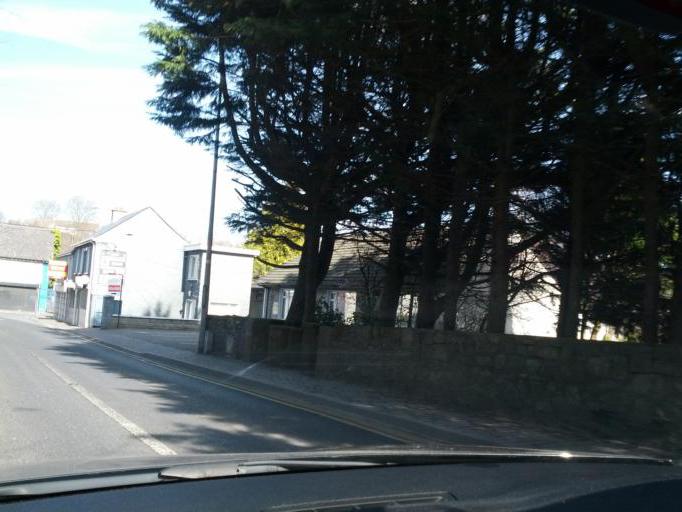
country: IE
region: Leinster
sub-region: Kildare
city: Leixlip
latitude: 53.3637
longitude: -6.4861
